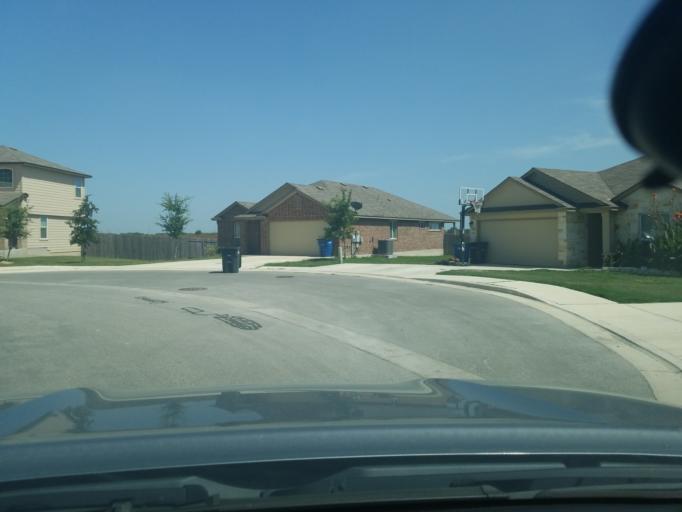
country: US
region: Texas
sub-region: Guadalupe County
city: Lake Dunlap
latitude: 29.6679
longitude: -98.0390
